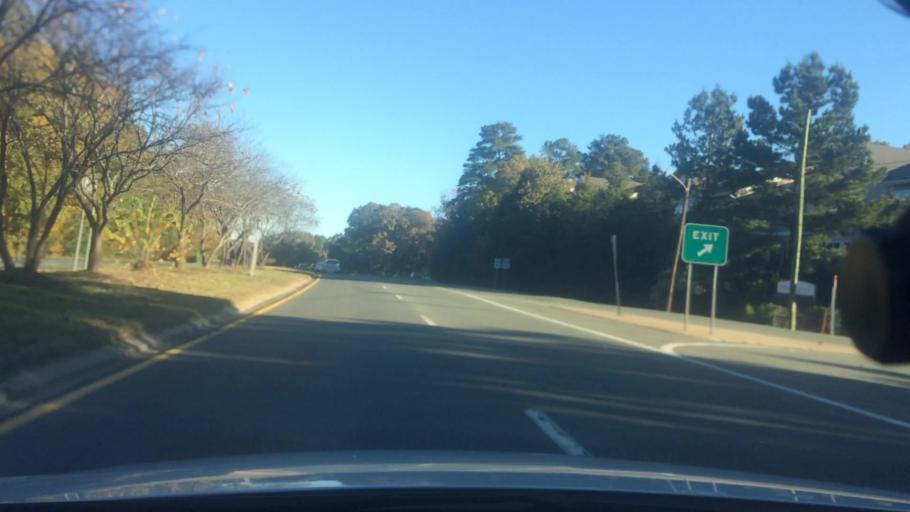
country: US
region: North Carolina
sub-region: Orange County
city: Chapel Hill
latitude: 35.9100
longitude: -79.0267
